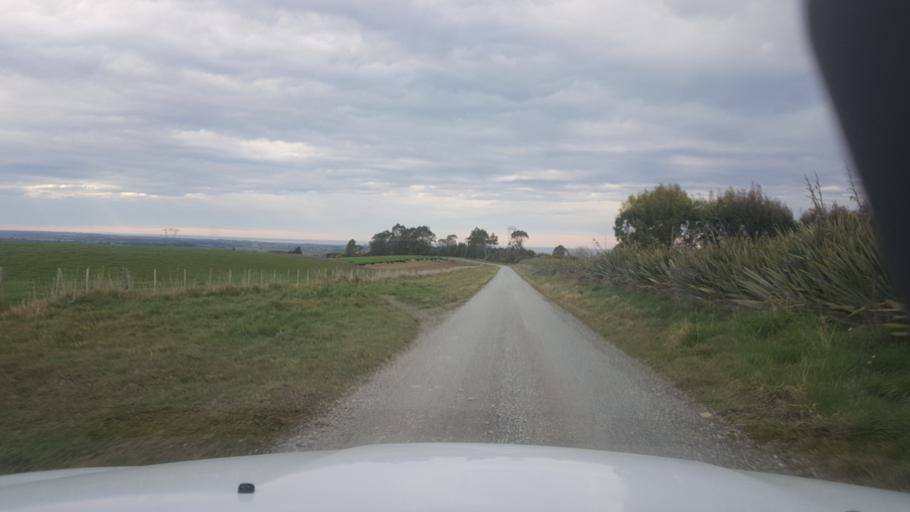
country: NZ
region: Canterbury
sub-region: Timaru District
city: Pleasant Point
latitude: -44.3456
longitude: 171.1286
